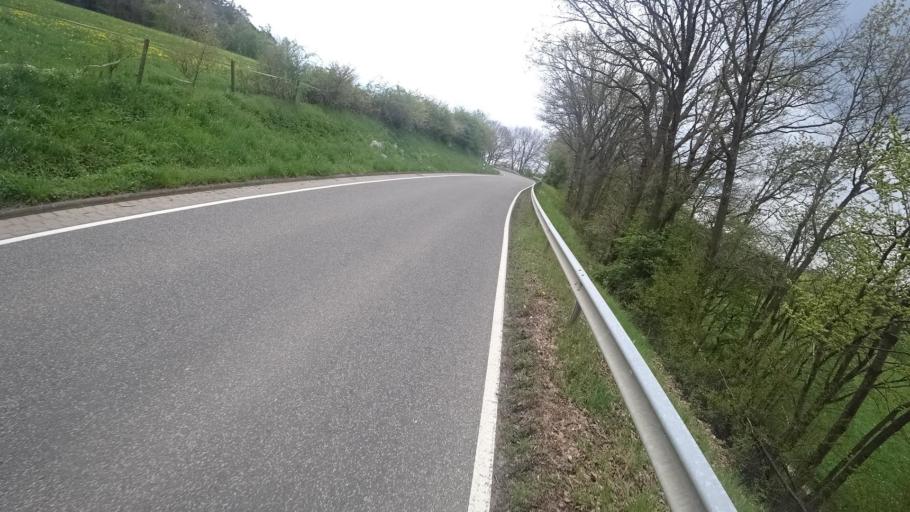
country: DE
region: Rheinland-Pfalz
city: Niederkumbd
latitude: 50.0053
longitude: 7.5357
